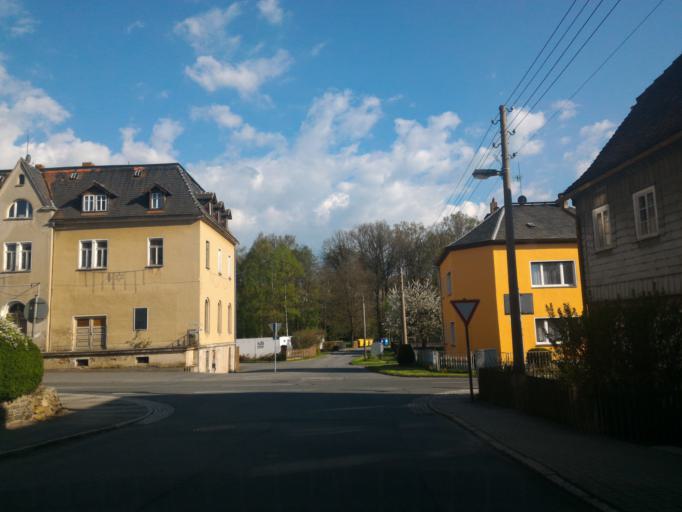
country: DE
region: Saxony
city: Seifhennersdorf
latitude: 50.9299
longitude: 14.6129
